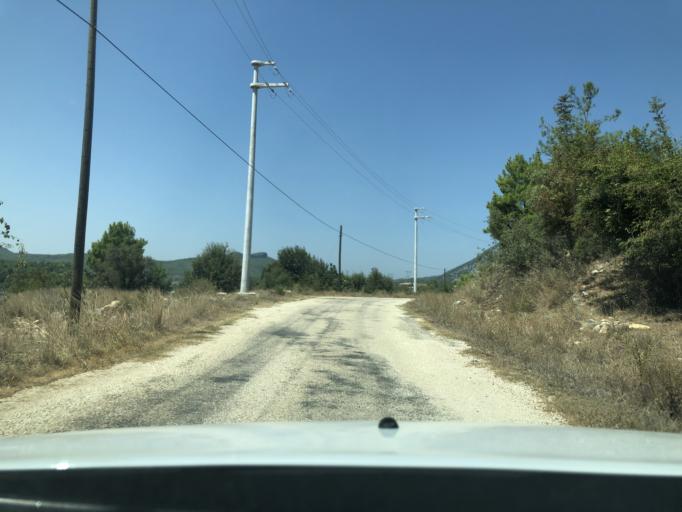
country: TR
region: Antalya
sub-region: Manavgat
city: Manavgat
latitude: 36.8732
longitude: 31.5507
